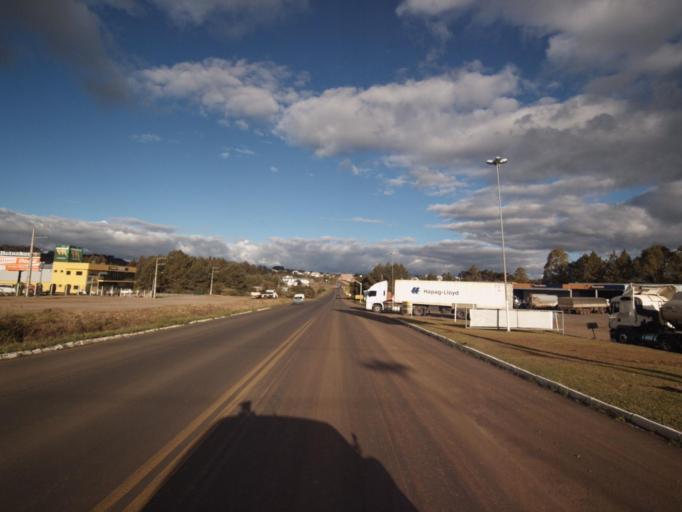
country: BR
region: Santa Catarina
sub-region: Campos Novos
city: Campos Novos
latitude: -27.3823
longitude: -51.2389
